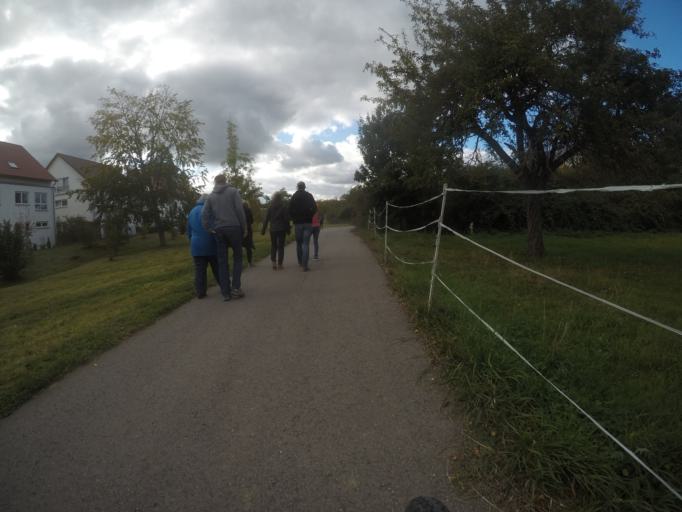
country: DE
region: Baden-Wuerttemberg
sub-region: Regierungsbezirk Stuttgart
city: Steinenbronn
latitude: 48.7328
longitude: 9.0957
